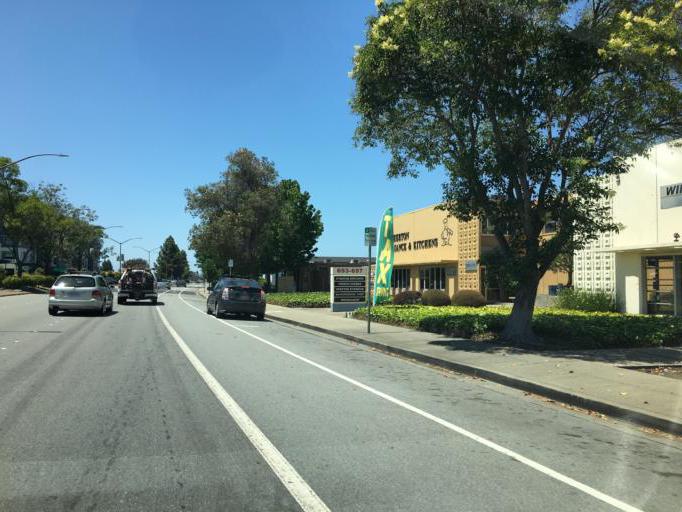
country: US
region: California
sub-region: San Mateo County
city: Redwood City
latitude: 37.4915
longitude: -122.2306
